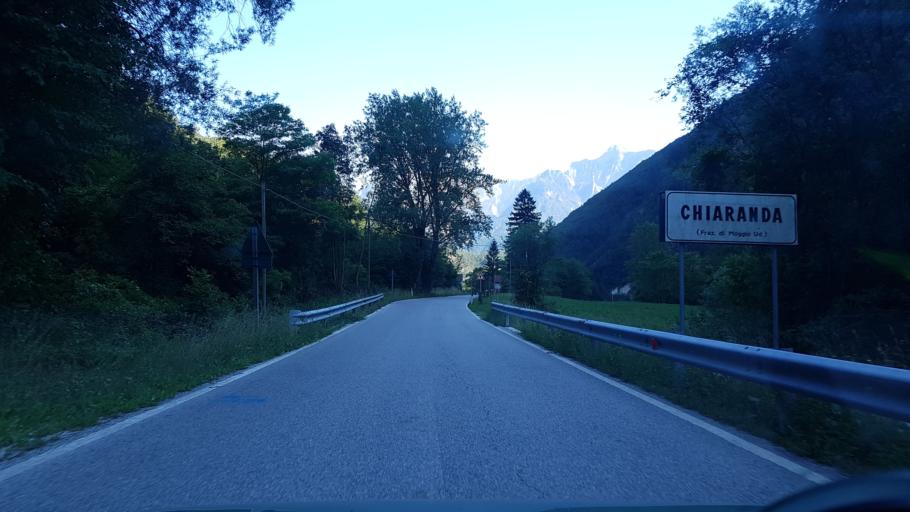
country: IT
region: Friuli Venezia Giulia
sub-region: Provincia di Udine
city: Moggio Udinese
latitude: 46.4353
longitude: 13.1986
